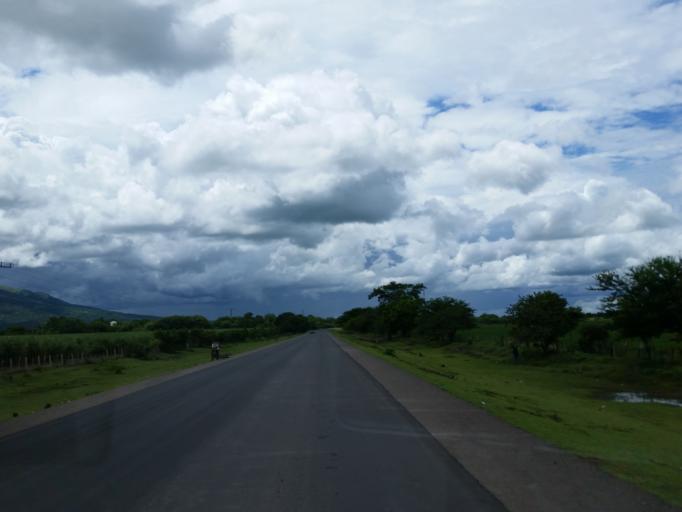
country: NI
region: Chinandega
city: Chichigalpa
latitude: 12.7880
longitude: -86.9305
